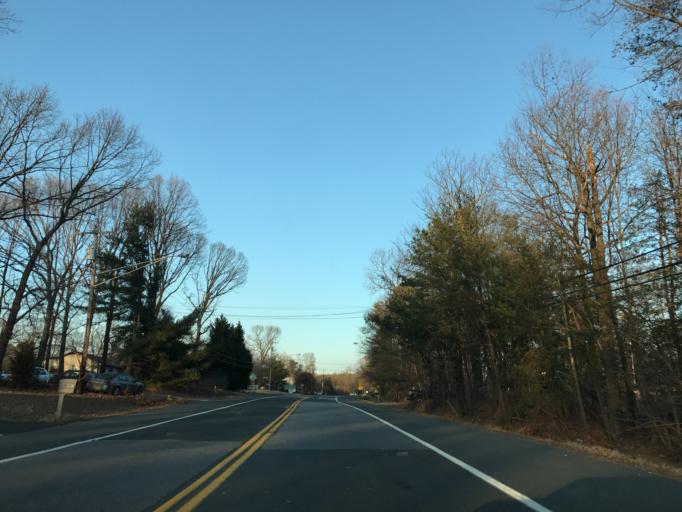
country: US
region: Maryland
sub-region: Anne Arundel County
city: Green Haven
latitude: 39.1106
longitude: -76.5258
